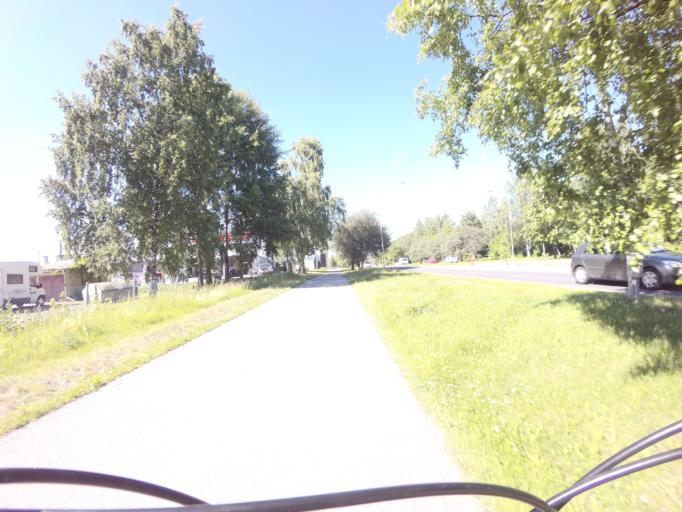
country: FI
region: Varsinais-Suomi
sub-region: Turku
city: Turku
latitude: 60.4704
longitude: 22.2656
